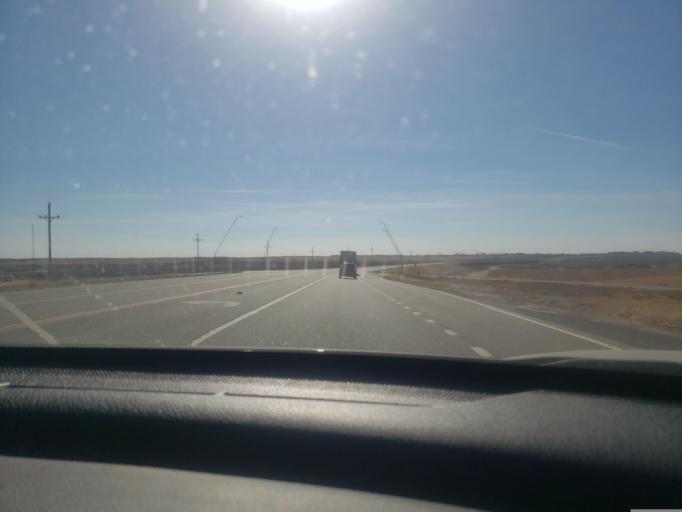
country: US
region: Kansas
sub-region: Finney County
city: Garden City
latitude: 37.9554
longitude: -100.8404
